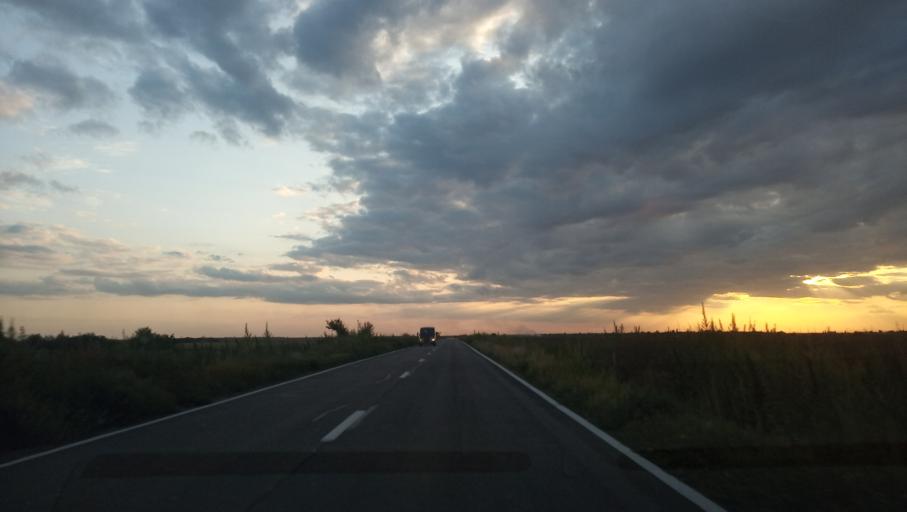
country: RO
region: Calarasi
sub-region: Comuna Vlad Tepes
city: Mihai Viteazu
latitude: 44.3621
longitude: 27.0333
